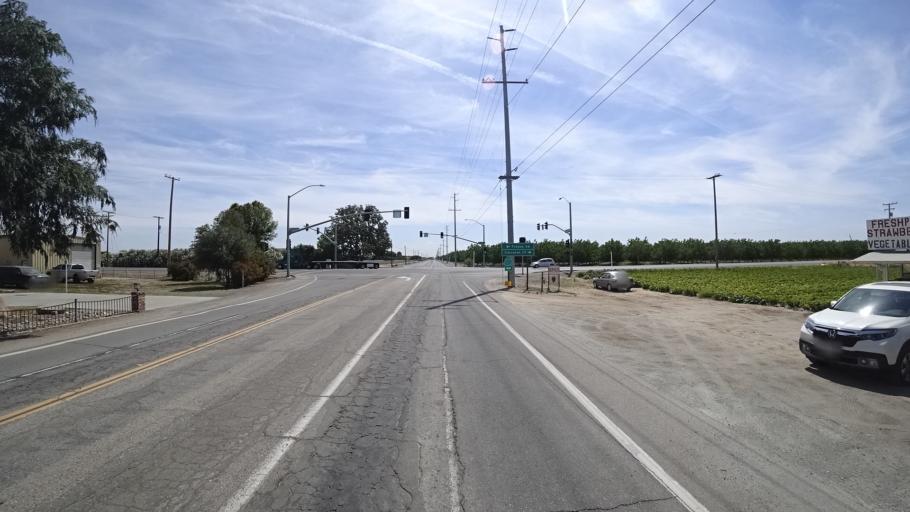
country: US
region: California
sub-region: Kings County
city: Hanford
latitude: 36.3425
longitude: -119.6015
